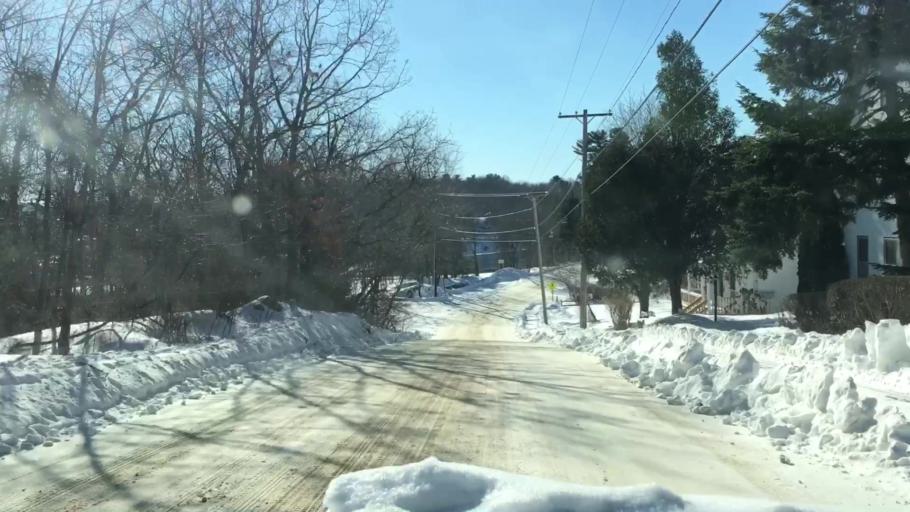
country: US
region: Maine
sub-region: Sagadahoc County
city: Topsham
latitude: 43.9193
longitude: -69.9734
